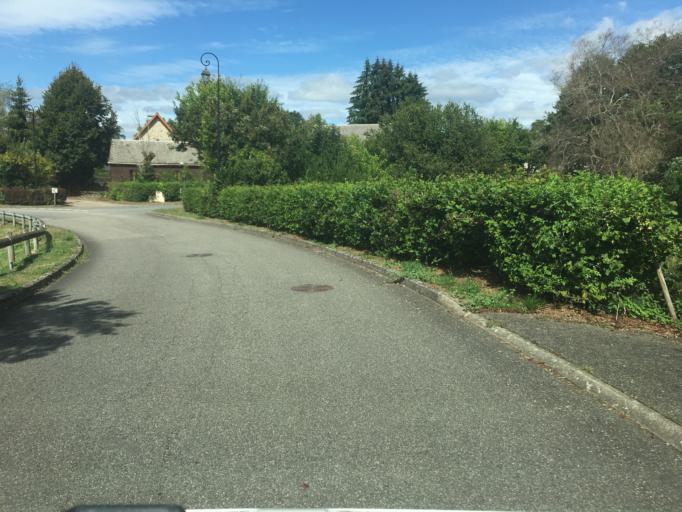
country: FR
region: Auvergne
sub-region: Departement du Cantal
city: Champagnac
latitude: 45.4218
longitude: 2.3832
